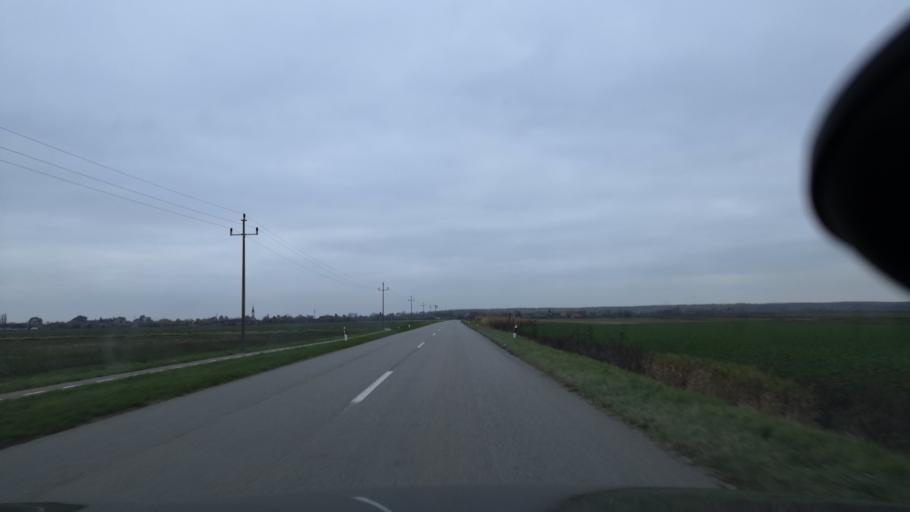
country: HU
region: Csongrad
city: Roszke
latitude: 46.1379
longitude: 20.0954
